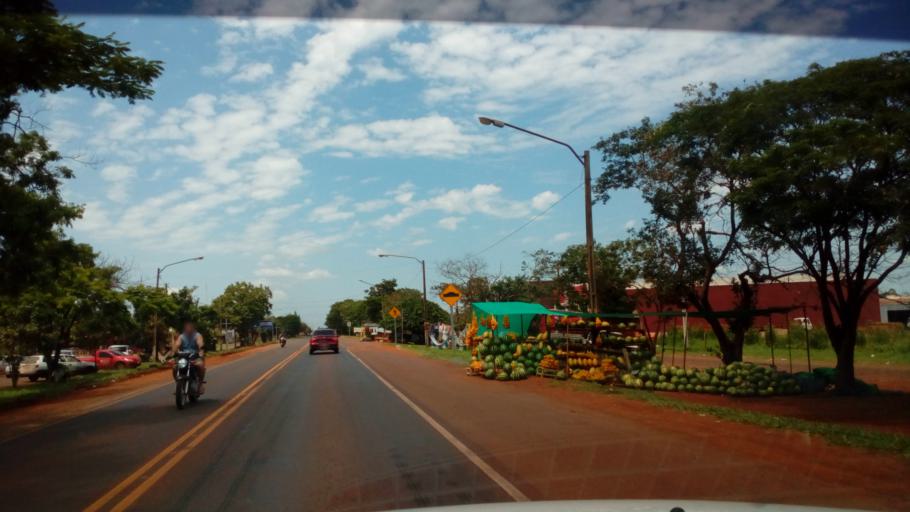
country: PY
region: Alto Parana
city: Santa Rita
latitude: -25.7806
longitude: -55.0775
